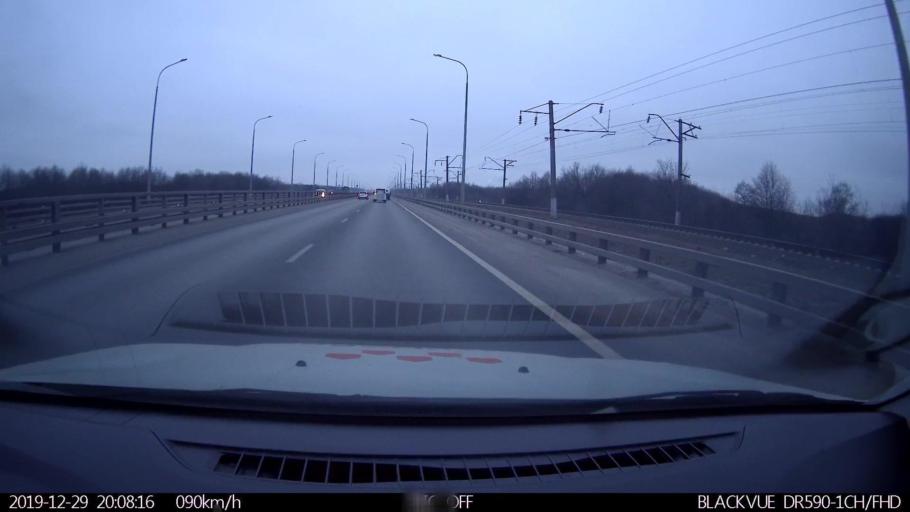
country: RU
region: Nizjnij Novgorod
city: Neklyudovo
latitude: 56.3879
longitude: 43.9701
